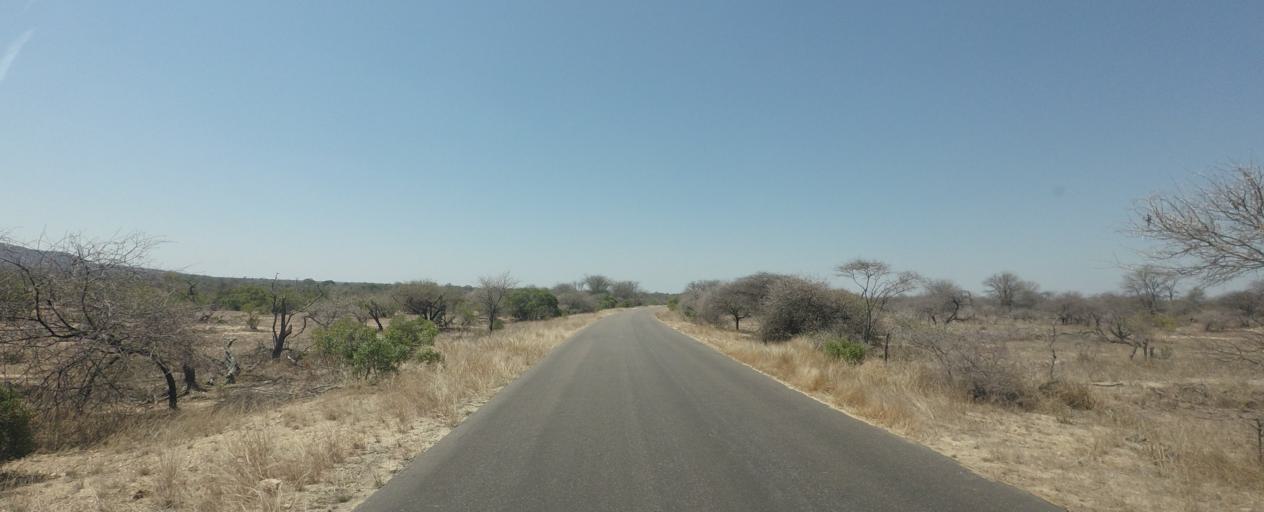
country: ZA
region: Limpopo
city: Thulamahashi
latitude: -24.4256
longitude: 31.5052
